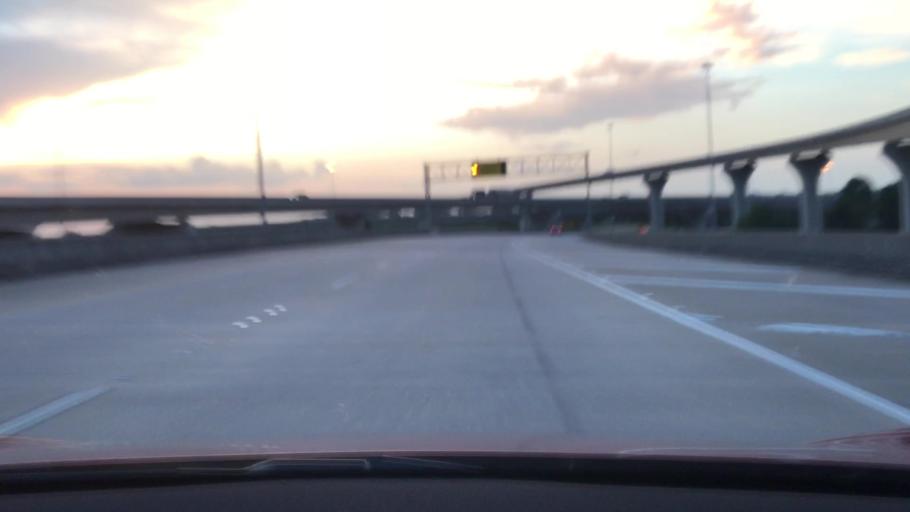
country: US
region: Louisiana
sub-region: Caddo Parish
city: Shreveport
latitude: 32.4944
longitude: -93.7581
